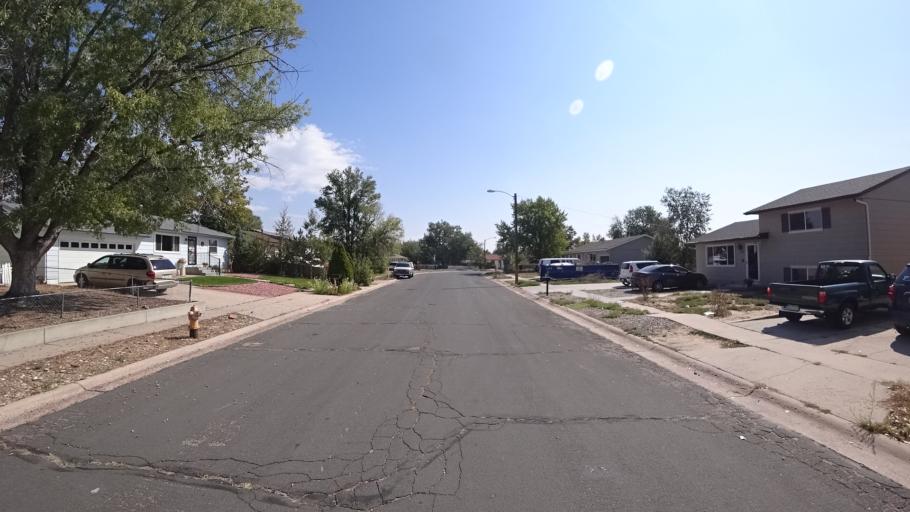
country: US
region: Colorado
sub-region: El Paso County
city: Colorado Springs
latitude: 38.8189
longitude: -104.7883
